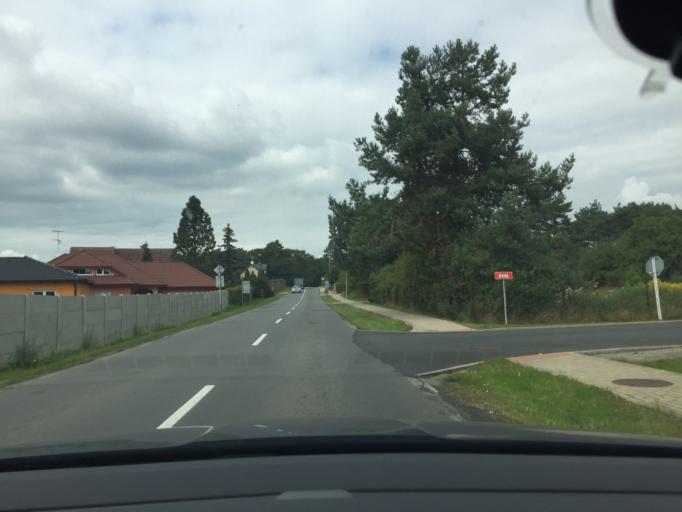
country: CZ
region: Ustecky
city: Roudnice nad Labem
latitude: 50.4437
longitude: 14.2606
